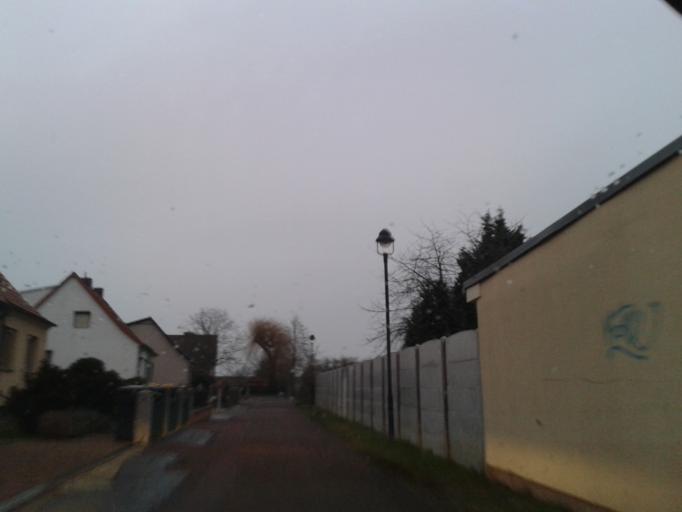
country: DE
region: Saxony-Anhalt
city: Peissen
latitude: 51.4947
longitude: 12.0296
